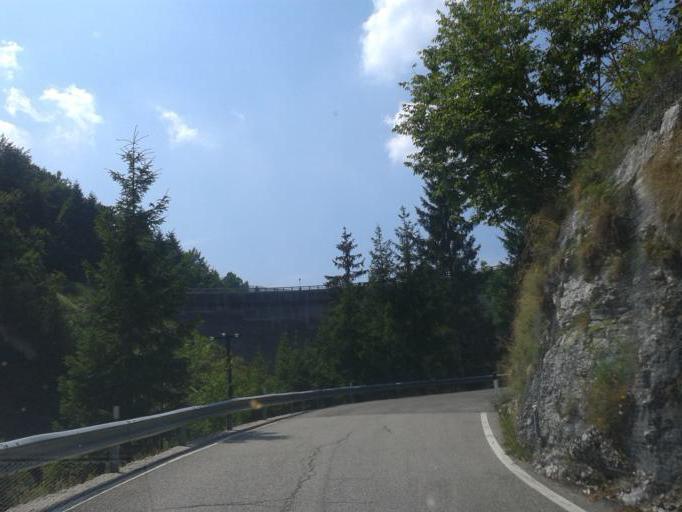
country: IT
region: Trentino-Alto Adige
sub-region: Provincia di Trento
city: Avio
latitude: 45.7716
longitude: 10.9048
